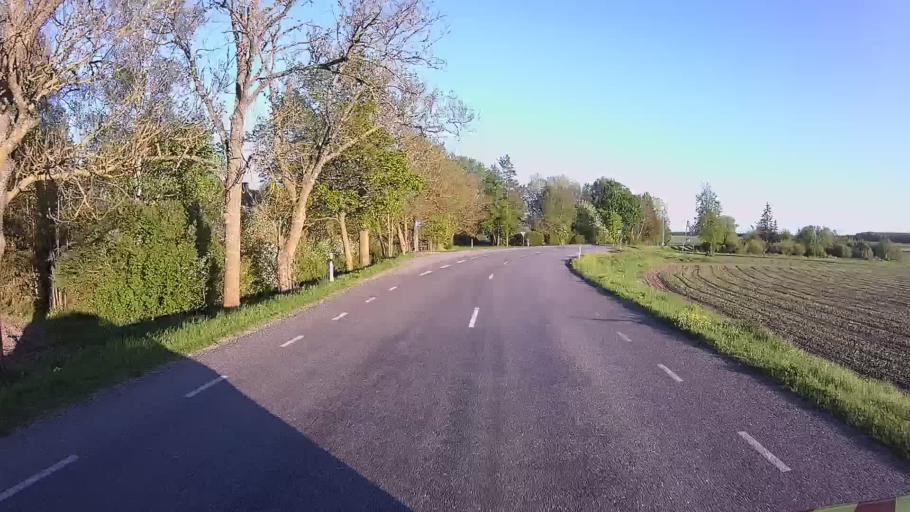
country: EE
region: Tartu
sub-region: Puhja vald
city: Puhja
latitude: 58.3243
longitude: 26.1899
